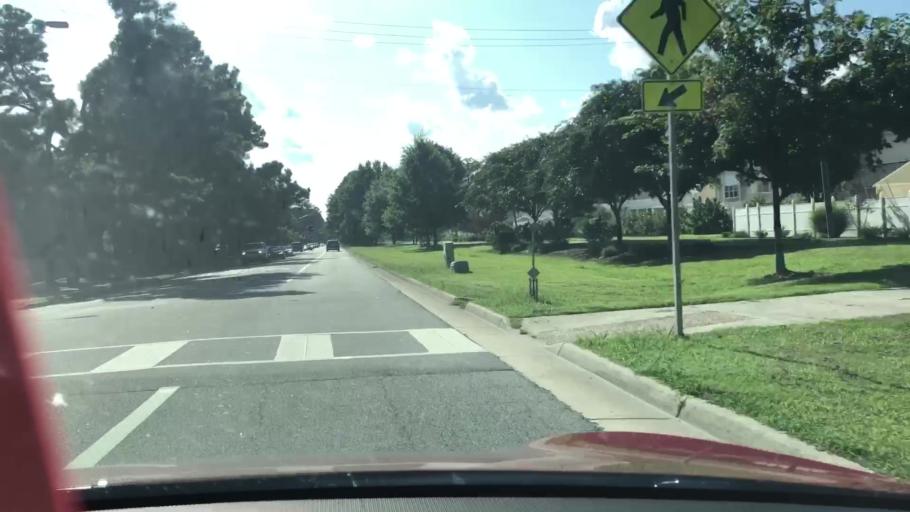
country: US
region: Virginia
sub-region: City of Virginia Beach
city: Virginia Beach
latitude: 36.8378
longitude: -75.9850
